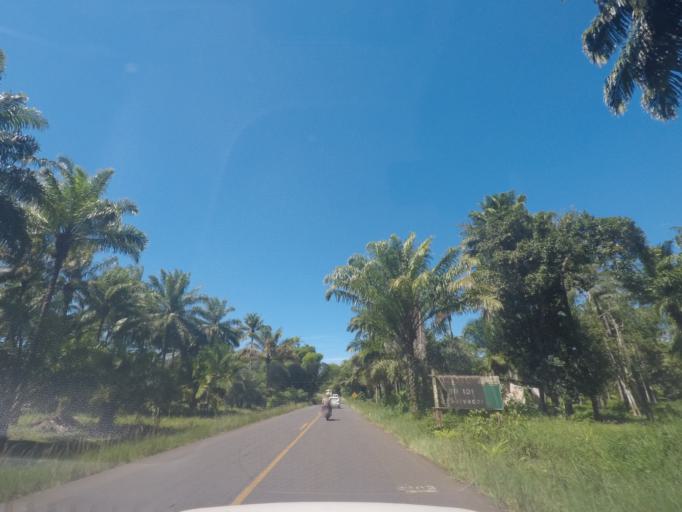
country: BR
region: Bahia
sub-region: Taperoa
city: Taperoa
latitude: -13.4695
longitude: -39.0882
